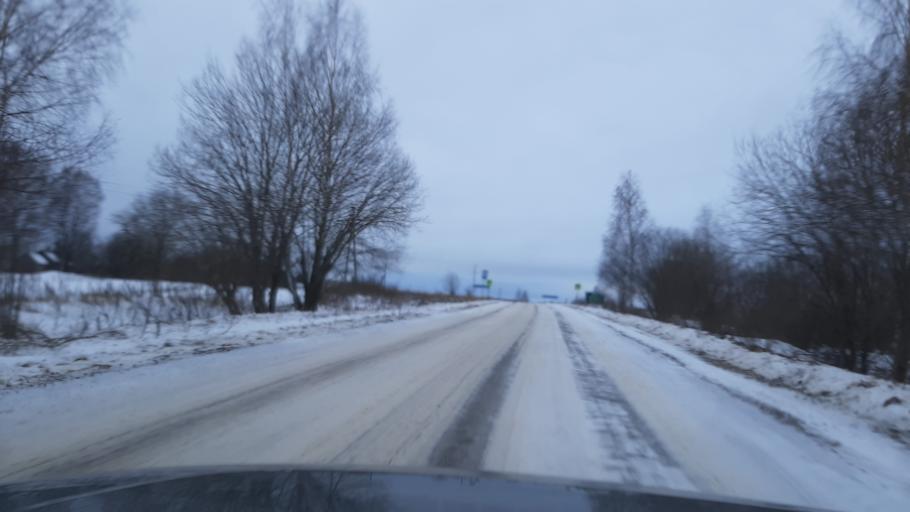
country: RU
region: Kostroma
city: Volgorechensk
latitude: 57.4390
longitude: 41.0932
